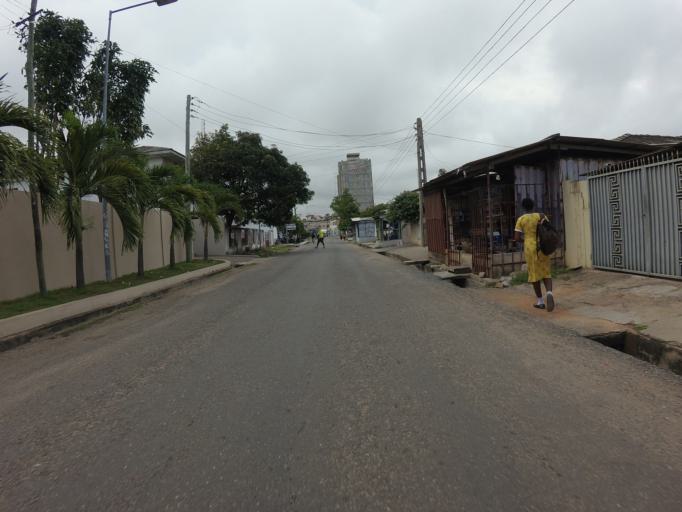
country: GH
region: Greater Accra
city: Accra
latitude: 5.5556
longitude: -0.1777
